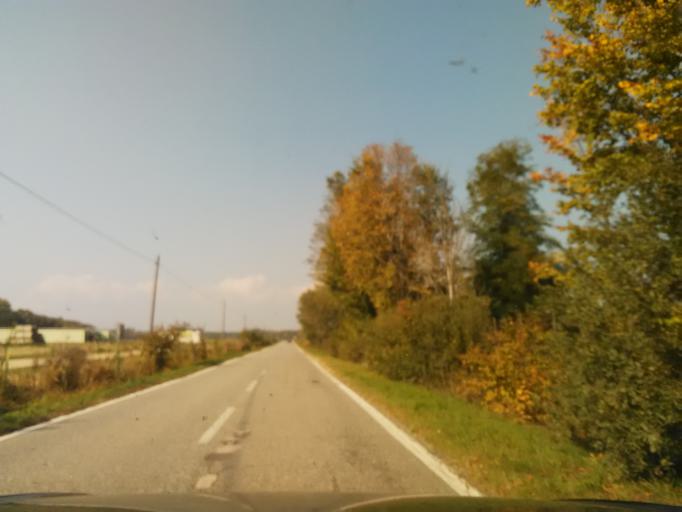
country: IT
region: Piedmont
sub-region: Provincia di Biella
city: Salussola
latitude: 45.4246
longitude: 8.1364
